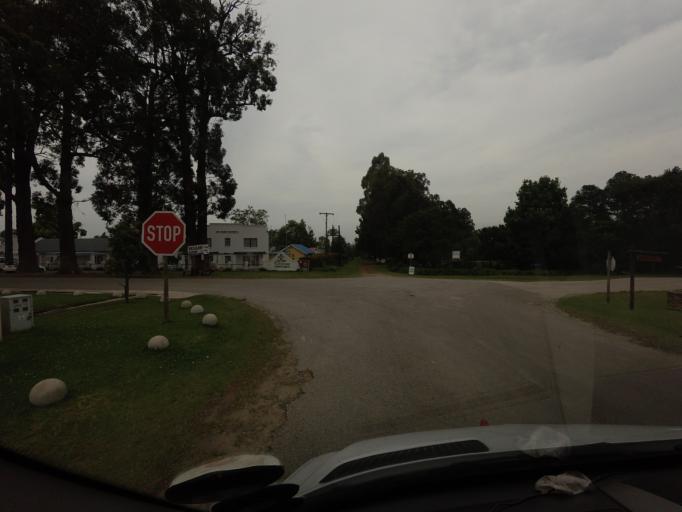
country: ZA
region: Eastern Cape
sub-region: Cacadu District Municipality
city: Kareedouw
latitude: -33.9732
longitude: 23.8860
